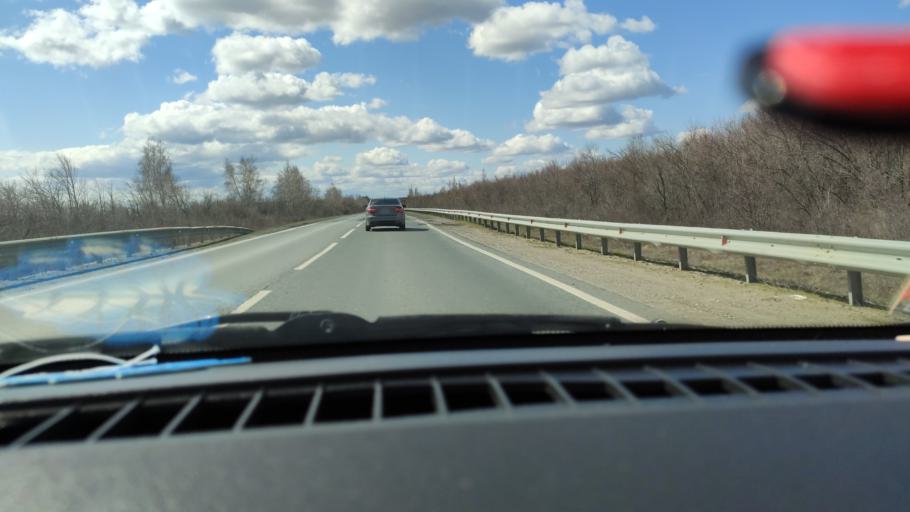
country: RU
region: Saratov
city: Dukhovnitskoye
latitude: 52.6719
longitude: 48.2230
